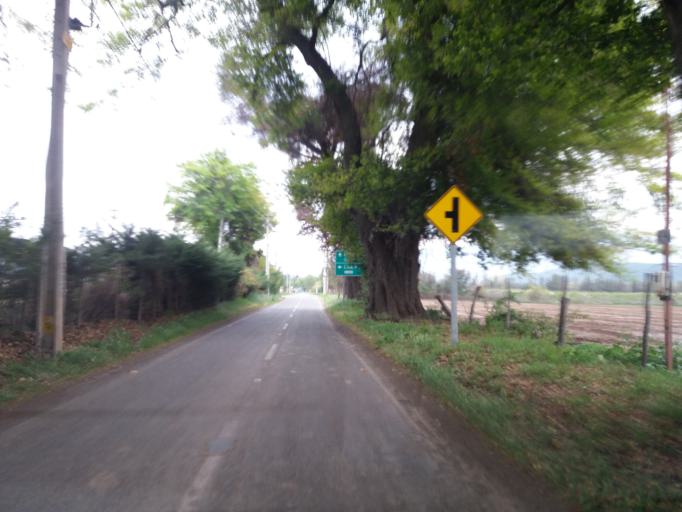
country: CL
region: Valparaiso
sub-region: Provincia de Quillota
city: Quillota
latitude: -32.8936
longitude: -71.1072
